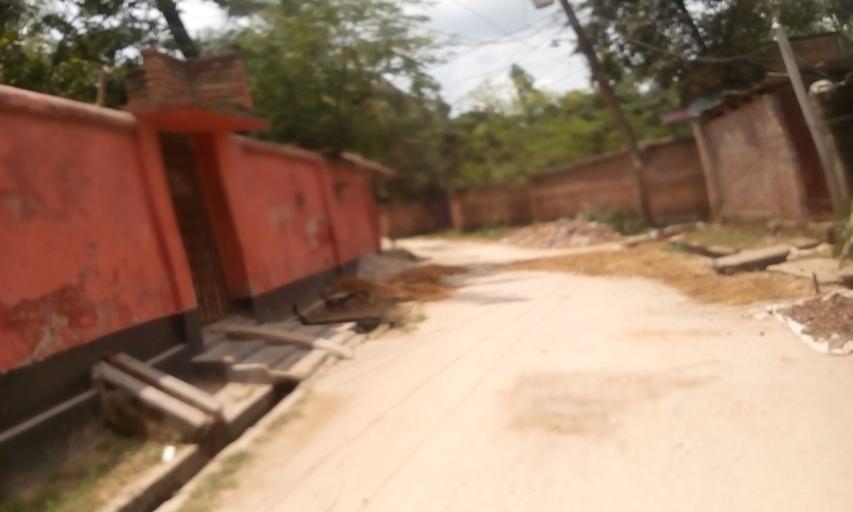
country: IN
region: West Bengal
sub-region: Dakshin Dinajpur
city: Balurghat
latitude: 25.3925
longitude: 88.9879
